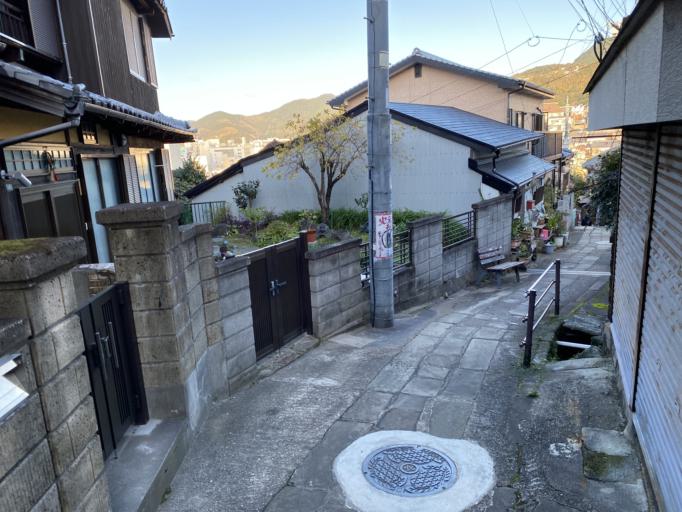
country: JP
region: Nagasaki
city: Nagasaki-shi
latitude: 32.7392
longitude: 129.8748
